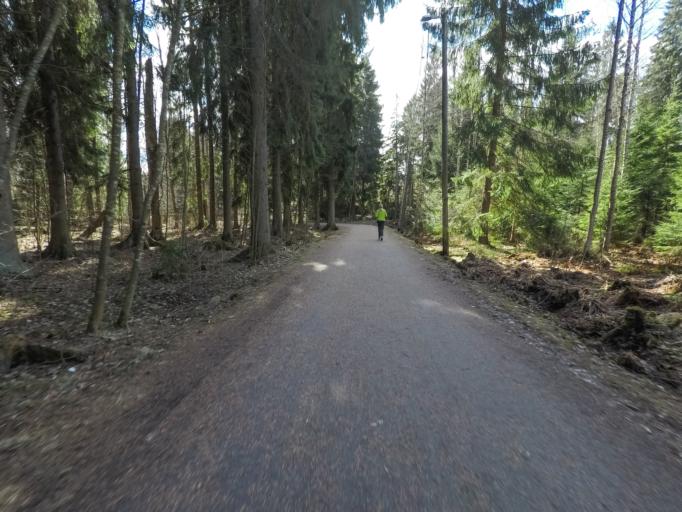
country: FI
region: Uusimaa
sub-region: Helsinki
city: Vantaa
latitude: 60.2225
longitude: 25.0484
